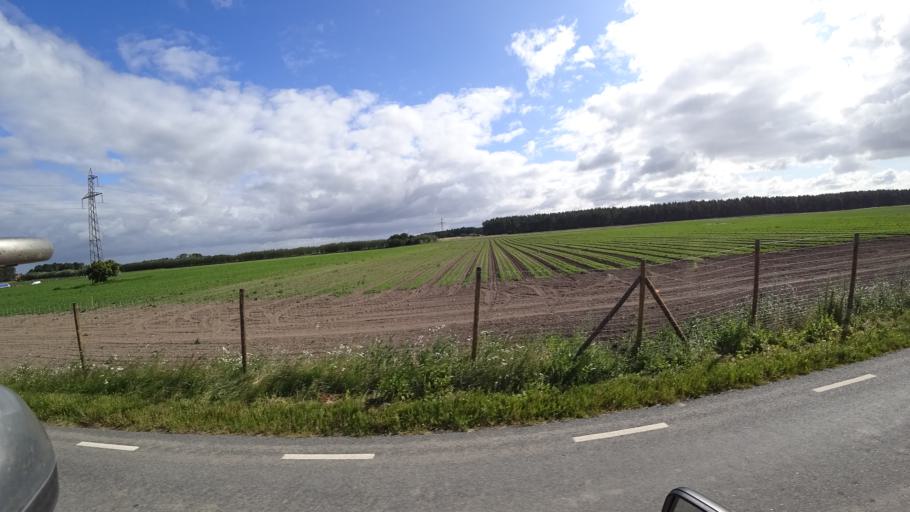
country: SE
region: Skane
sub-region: Kristianstads Kommun
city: Degeberga
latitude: 55.8747
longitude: 14.0418
